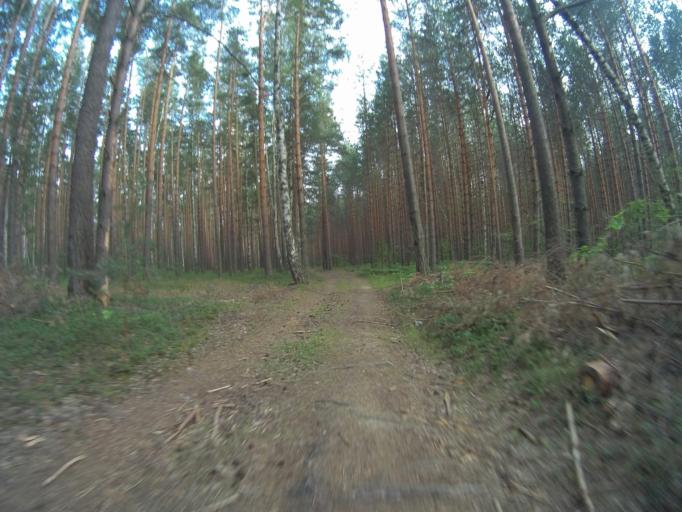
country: RU
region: Vladimir
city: Vorsha
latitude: 56.0080
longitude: 40.0990
